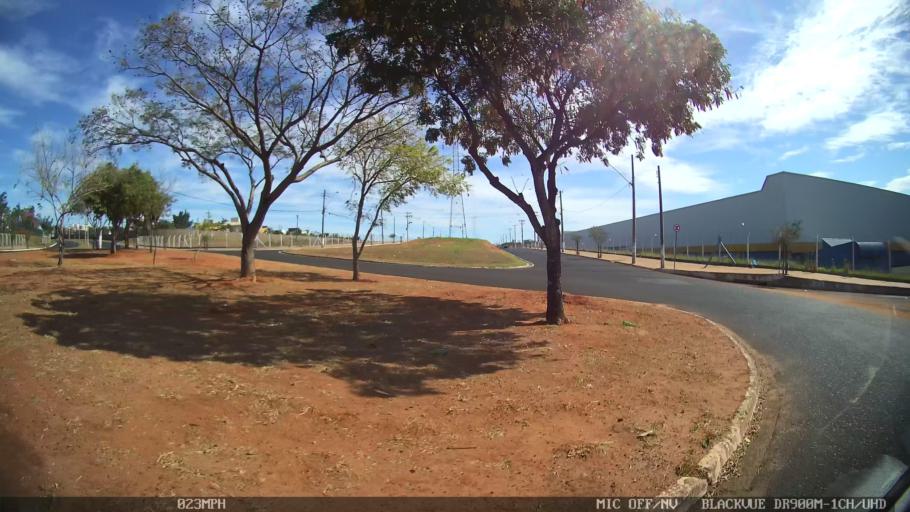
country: BR
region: Sao Paulo
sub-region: Sao Jose Do Rio Preto
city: Sao Jose do Rio Preto
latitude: -20.8185
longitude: -49.4796
